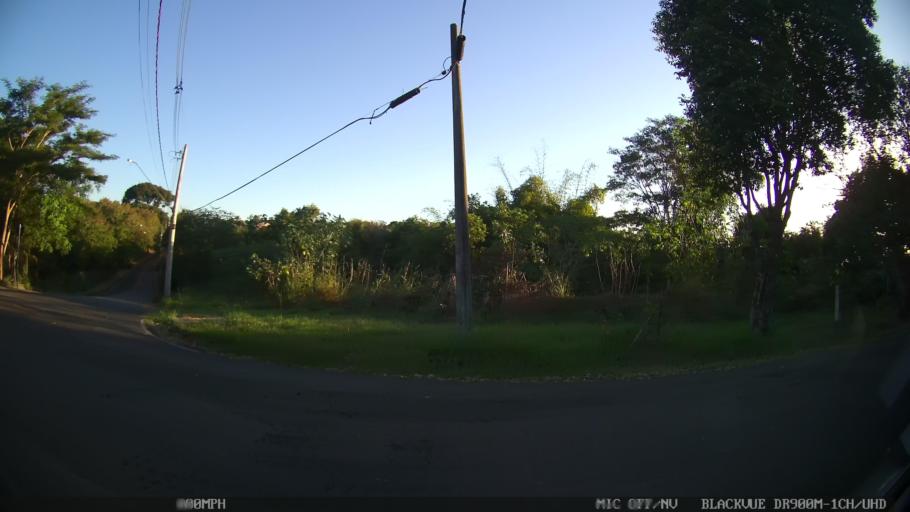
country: BR
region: Sao Paulo
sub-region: Sao Jose Do Rio Preto
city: Sao Jose do Rio Preto
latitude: -20.7729
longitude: -49.3548
